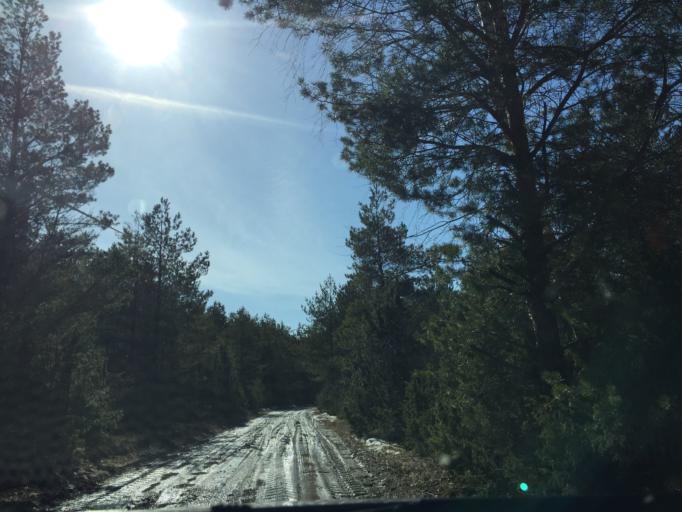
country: EE
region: Laeaene
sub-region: Haapsalu linn
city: Haapsalu
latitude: 58.6414
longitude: 23.5170
